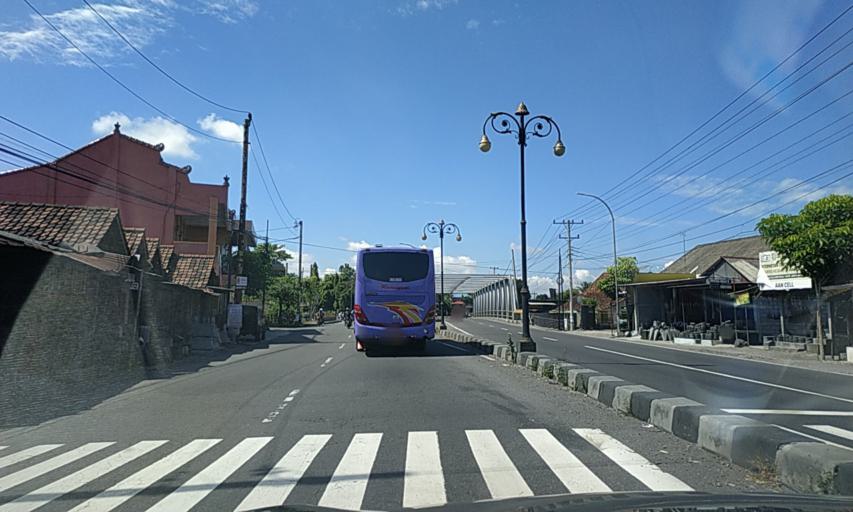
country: ID
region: Central Java
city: Muntilan
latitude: -7.5761
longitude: 110.2637
